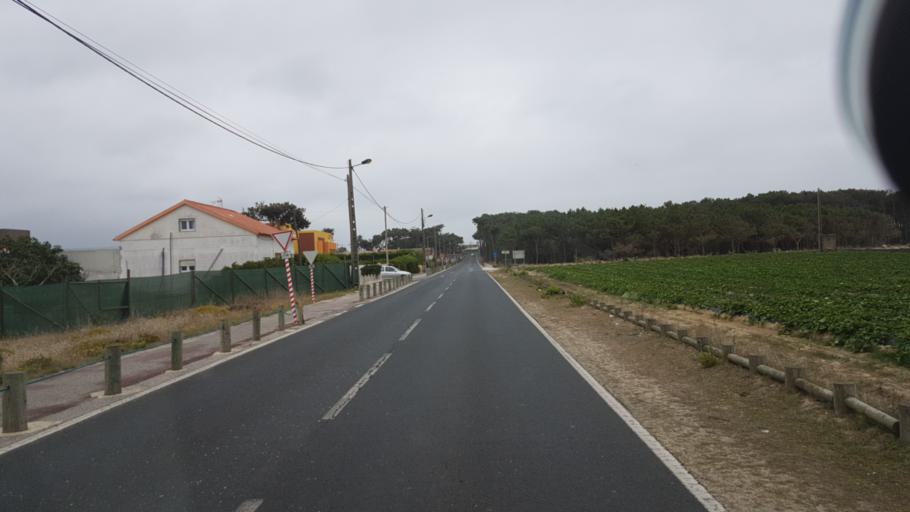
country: PT
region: Lisbon
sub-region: Torres Vedras
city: Silveira
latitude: 39.1585
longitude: -9.3616
